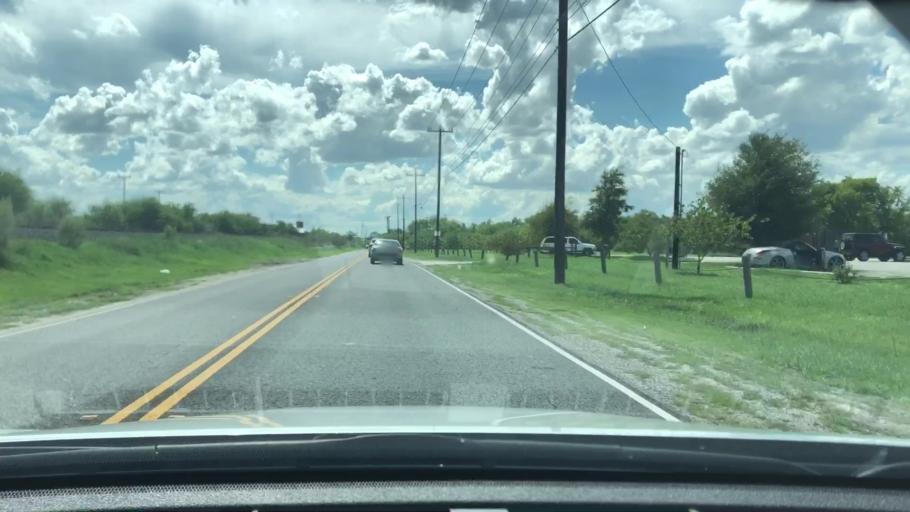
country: US
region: Texas
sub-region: Bexar County
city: Kirby
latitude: 29.4857
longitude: -98.3662
